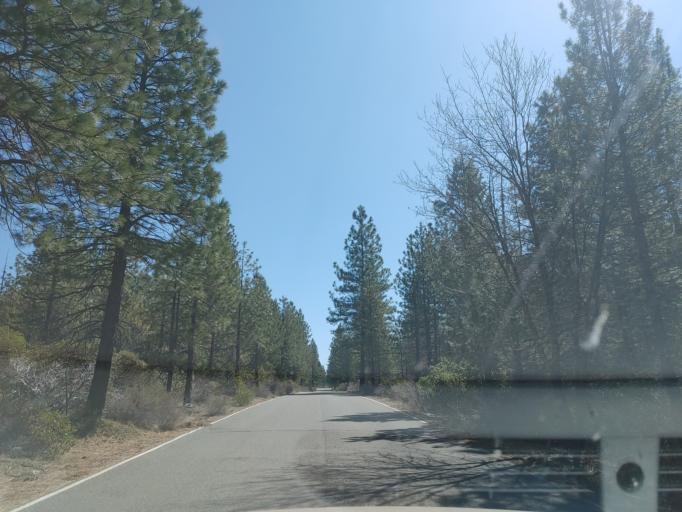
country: US
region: California
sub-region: Siskiyou County
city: McCloud
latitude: 41.2453
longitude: -122.0143
